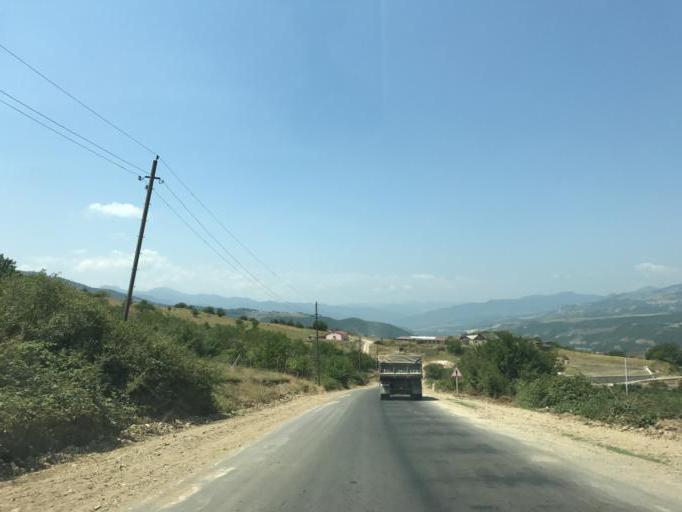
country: AZ
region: Tartar Rayon
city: Martakert
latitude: 40.1451
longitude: 46.6181
